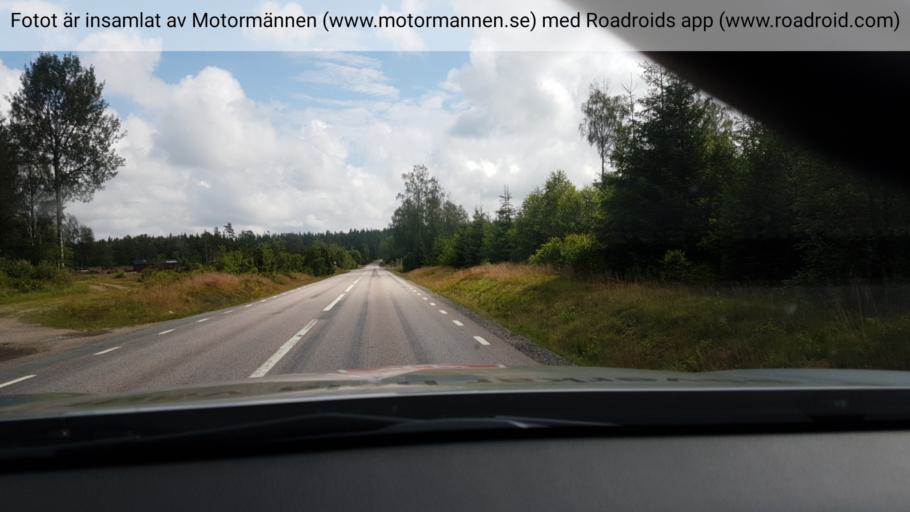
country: SE
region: Vaestra Goetaland
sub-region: Marks Kommun
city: Fritsla
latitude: 57.5004
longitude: 12.9105
